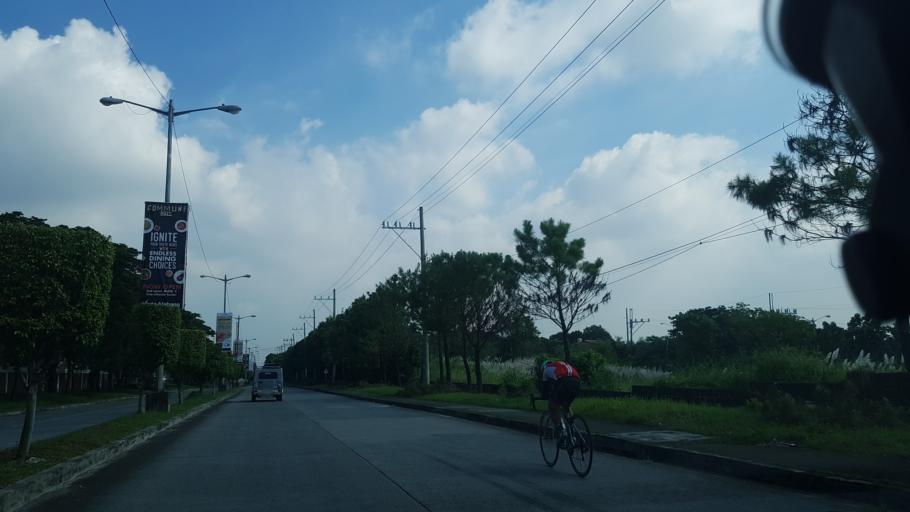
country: PH
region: Calabarzon
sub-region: Province of Laguna
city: Magsaysay
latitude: 14.3579
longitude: 121.0094
